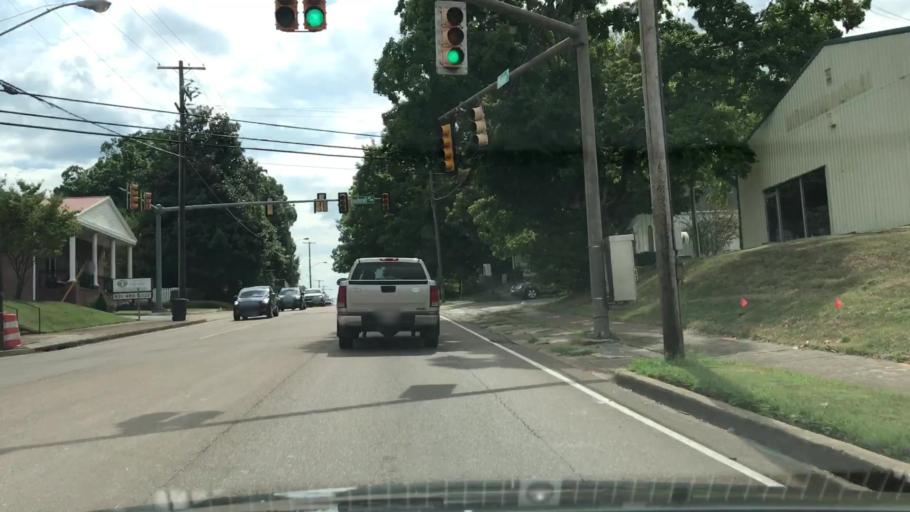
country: US
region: Tennessee
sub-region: Maury County
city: Spring Hill
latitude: 35.7528
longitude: -86.9287
